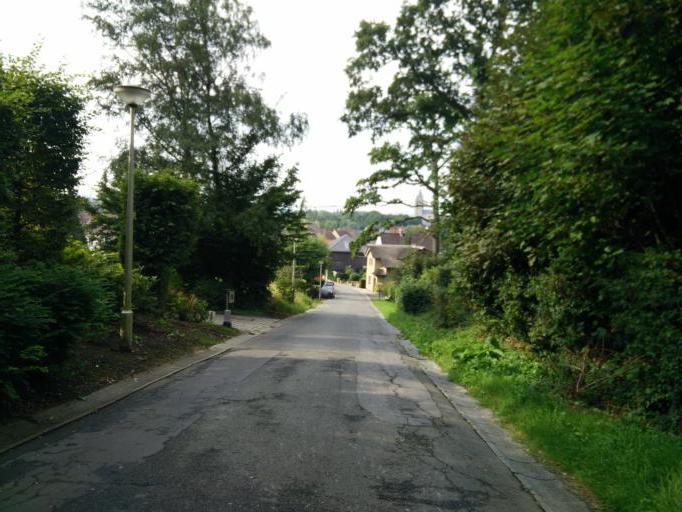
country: BE
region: Flanders
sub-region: Provincie Oost-Vlaanderen
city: Oudenaarde
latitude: 50.8336
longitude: 3.6094
